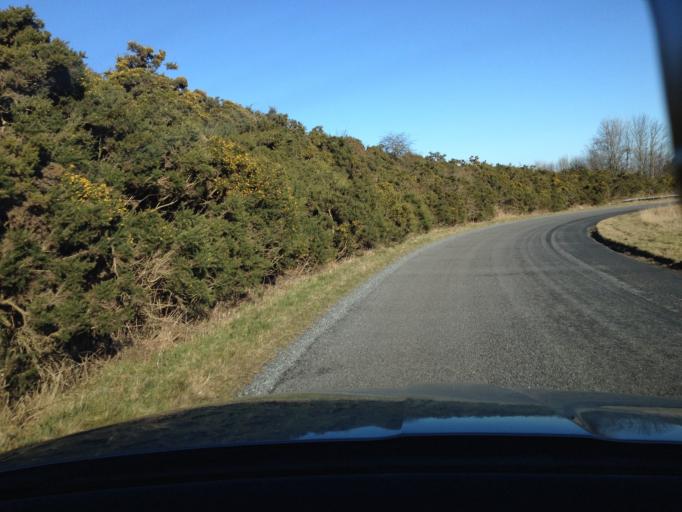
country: GB
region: Scotland
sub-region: Perth and Kinross
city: Bridge of Earn
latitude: 56.3149
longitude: -3.3739
